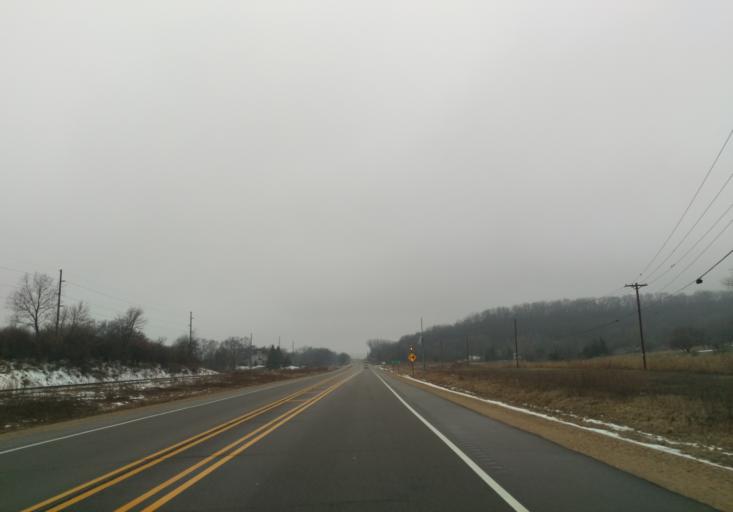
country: US
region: Wisconsin
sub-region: Dane County
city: Cross Plains
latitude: 43.0961
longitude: -89.6152
